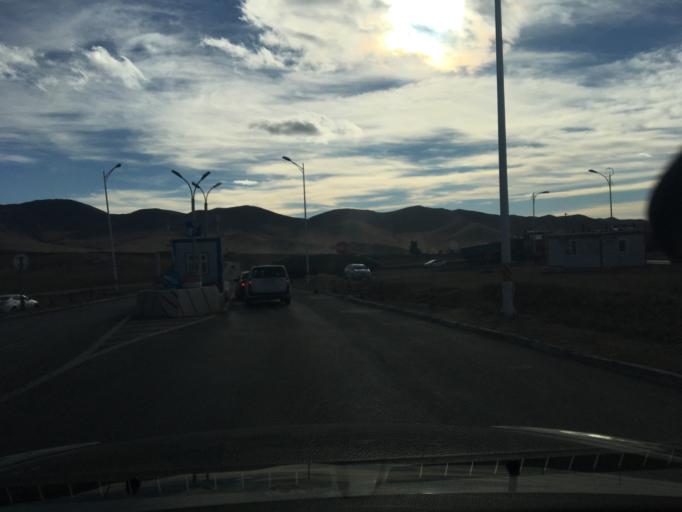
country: MN
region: Ulaanbaatar
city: Ulaanbaatar
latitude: 47.7777
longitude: 106.7420
